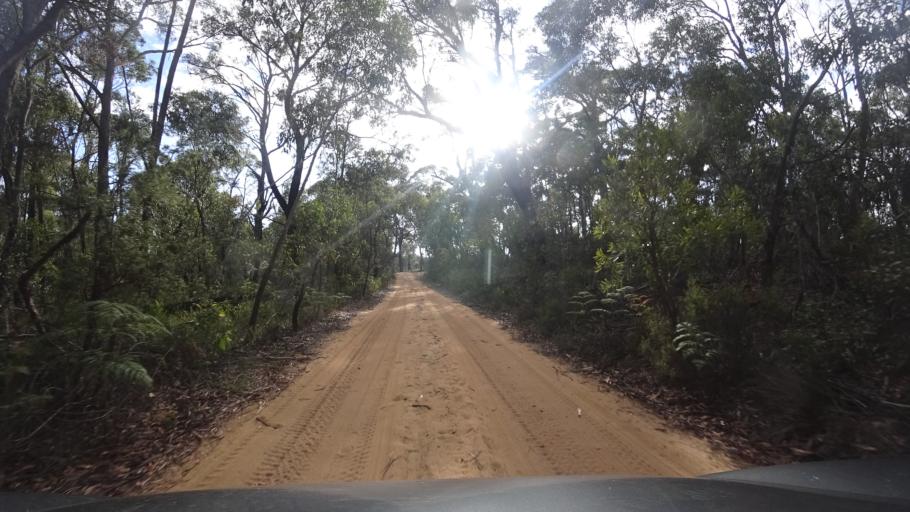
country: AU
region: New South Wales
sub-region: Lithgow
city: Lithgow
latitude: -33.4837
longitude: 150.2461
